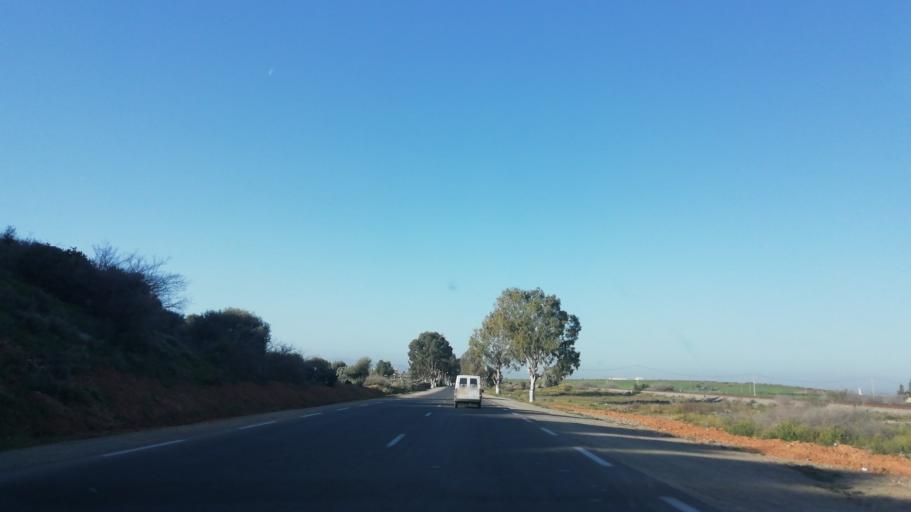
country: DZ
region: Mascara
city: Mascara
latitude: 35.6496
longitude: 0.1709
